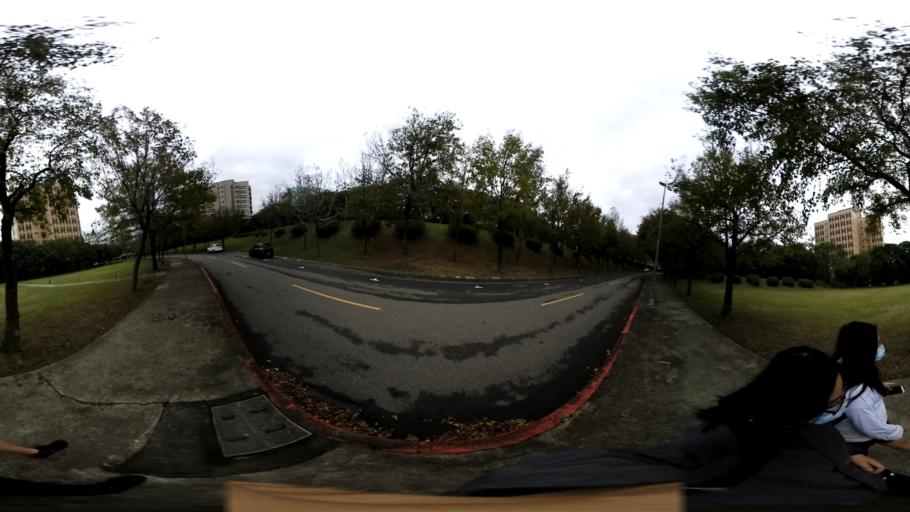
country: TW
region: Taiwan
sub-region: Hsinchu
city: Hsinchu
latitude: 24.7839
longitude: 120.9993
